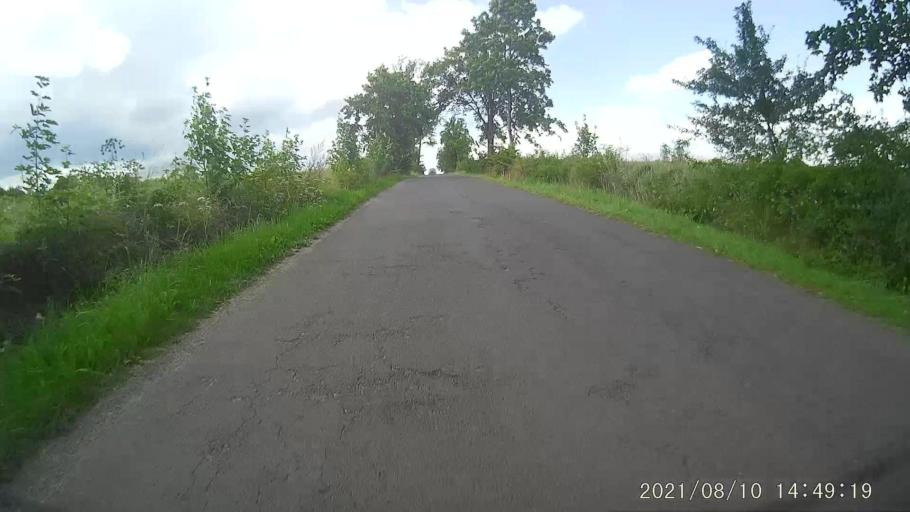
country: PL
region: Lower Silesian Voivodeship
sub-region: Powiat klodzki
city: Radkow
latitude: 50.5100
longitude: 16.4054
